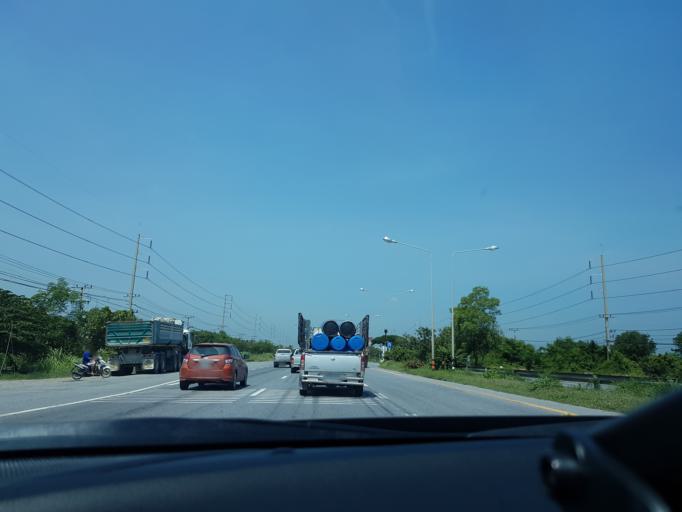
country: TH
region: Sara Buri
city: Saraburi
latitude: 14.5101
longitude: 100.9045
